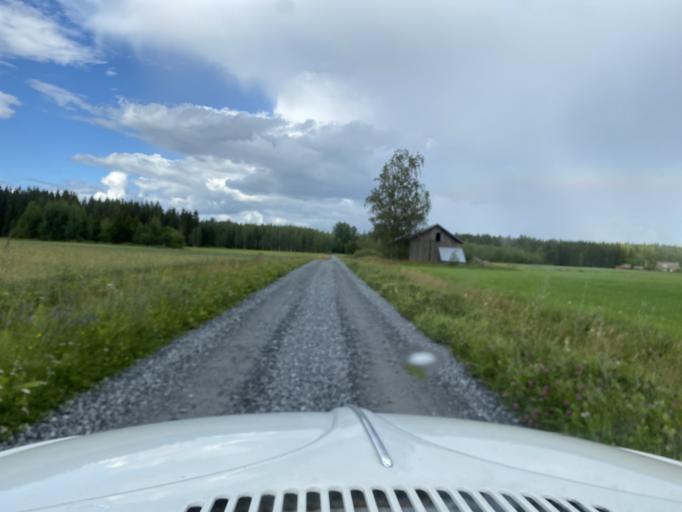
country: FI
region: Pirkanmaa
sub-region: Lounais-Pirkanmaa
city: Punkalaidun
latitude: 61.1318
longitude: 23.0664
